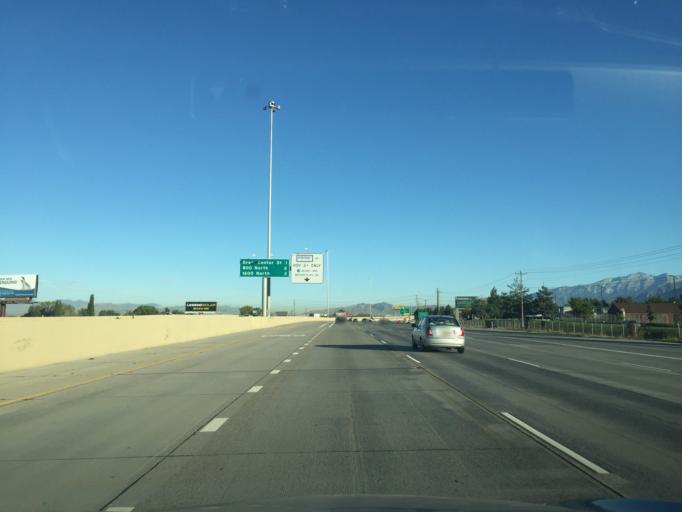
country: US
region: Utah
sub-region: Utah County
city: Orem
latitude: 40.2794
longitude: -111.7223
